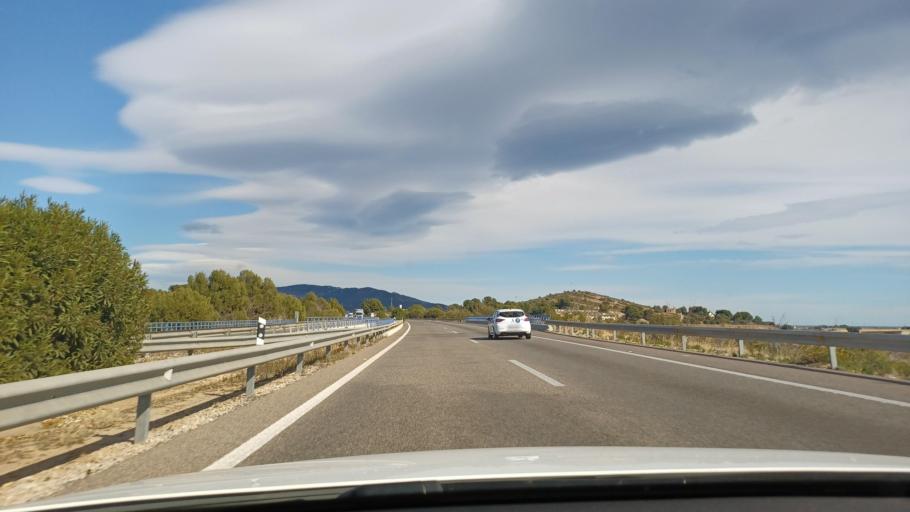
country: ES
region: Valencia
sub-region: Provincia de Castello
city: Torreblanca
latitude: 40.2291
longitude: 0.2048
